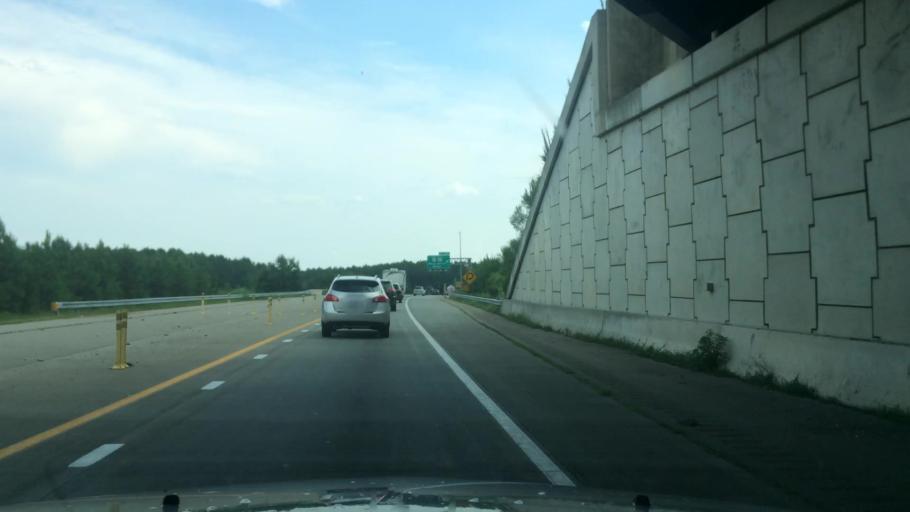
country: US
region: North Carolina
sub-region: Wake County
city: Knightdale
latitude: 35.7690
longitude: -78.5064
